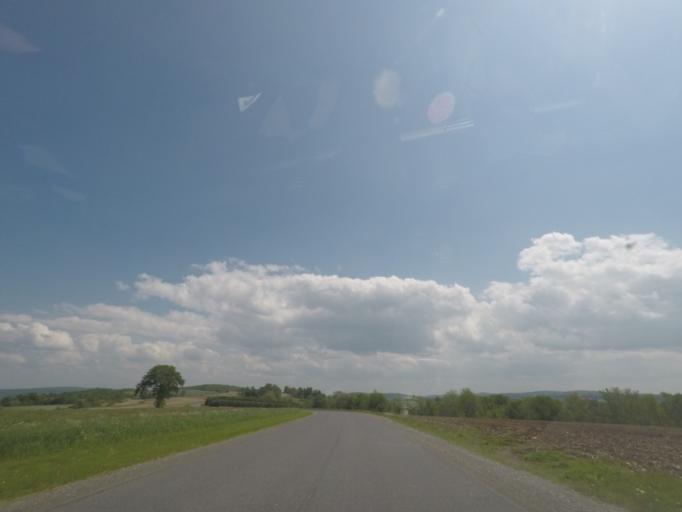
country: US
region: New York
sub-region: Dutchess County
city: Pine Plains
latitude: 41.9780
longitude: -73.5503
